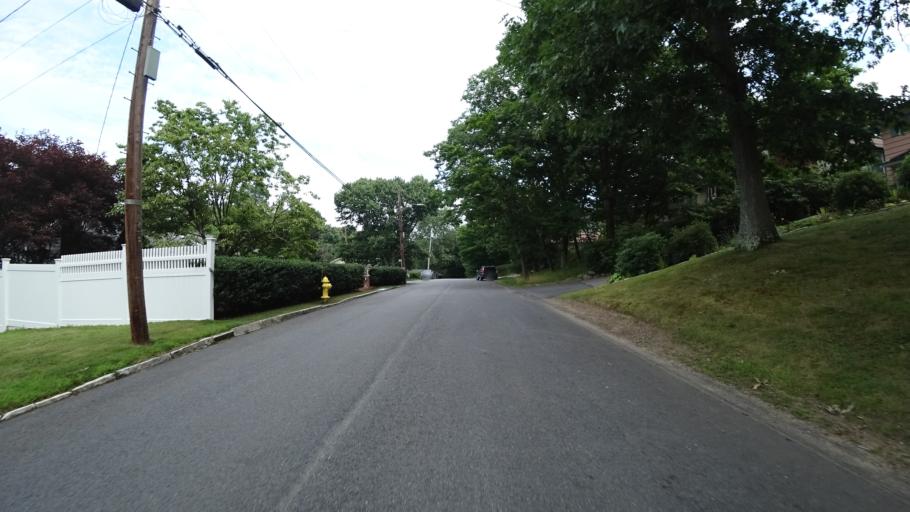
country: US
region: Massachusetts
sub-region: Norfolk County
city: Dedham
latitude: 42.2367
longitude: -71.1863
